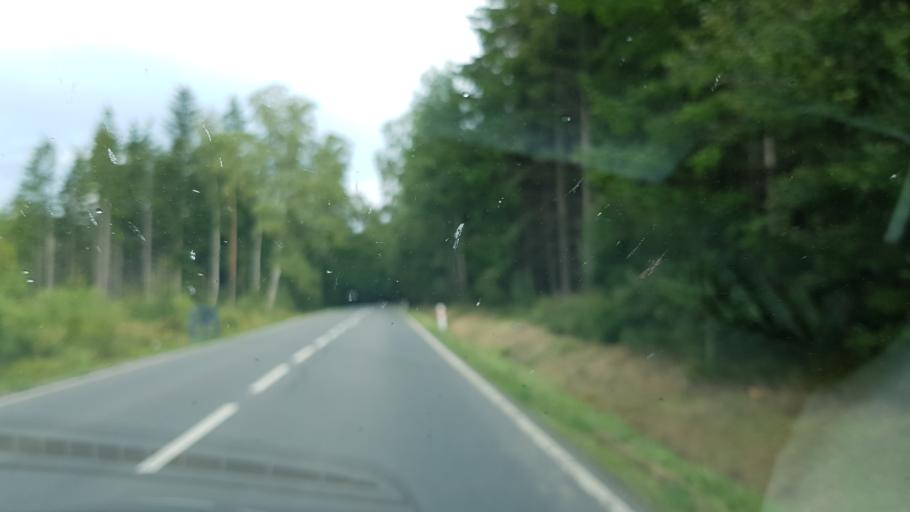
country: CZ
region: Pardubicky
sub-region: Okres Usti nad Orlici
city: Kraliky
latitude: 50.1022
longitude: 16.7839
